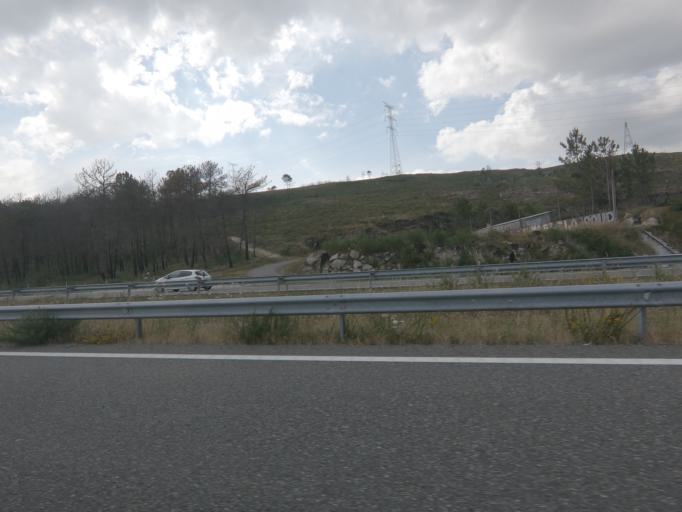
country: ES
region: Galicia
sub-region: Provincia de Ourense
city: Melon
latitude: 42.2628
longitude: -8.2123
